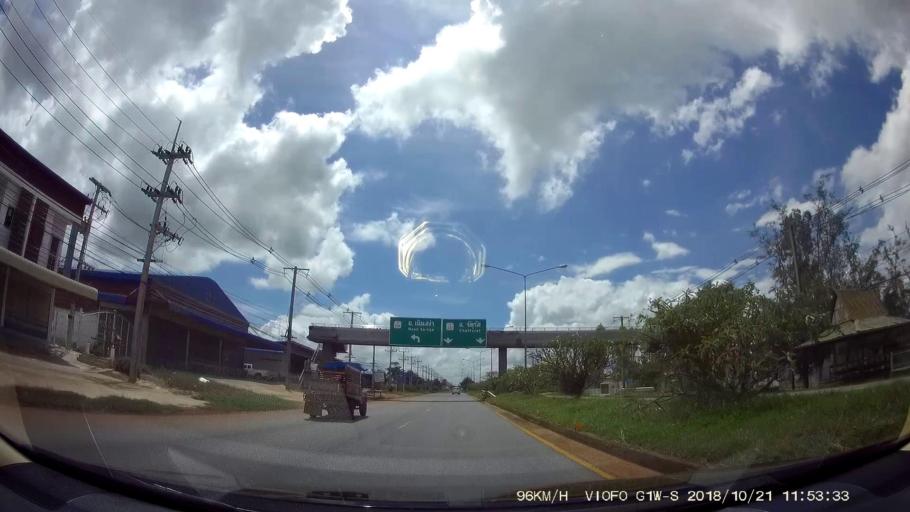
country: TH
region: Chaiyaphum
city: Chatturat
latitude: 15.5943
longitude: 101.9054
